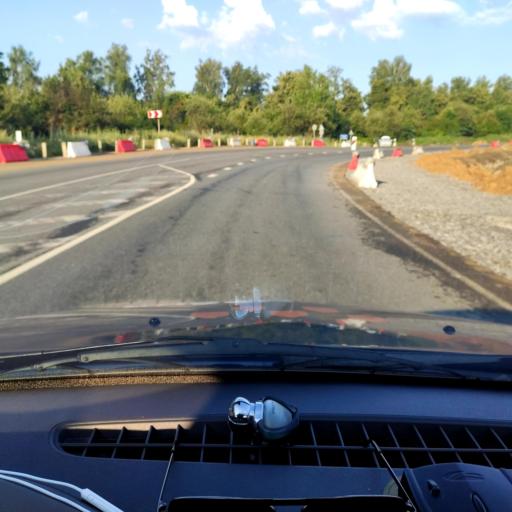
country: RU
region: Lipetsk
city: Kazaki
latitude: 52.5139
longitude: 38.1105
